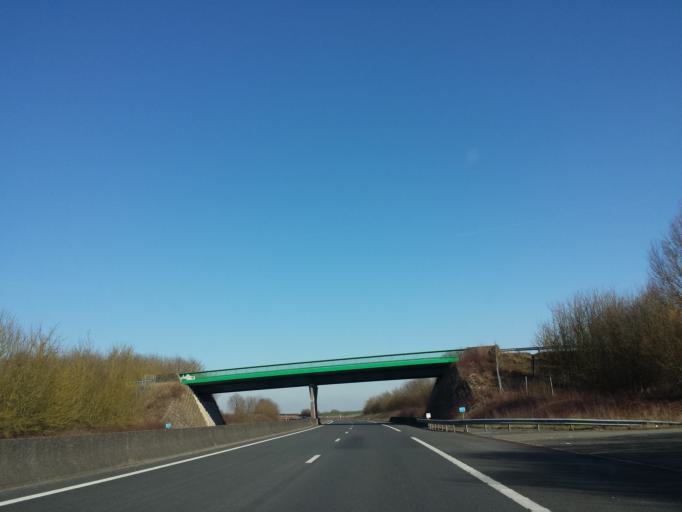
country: FR
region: Picardie
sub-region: Departement de l'Oise
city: Tille
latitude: 49.5151
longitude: 2.1851
